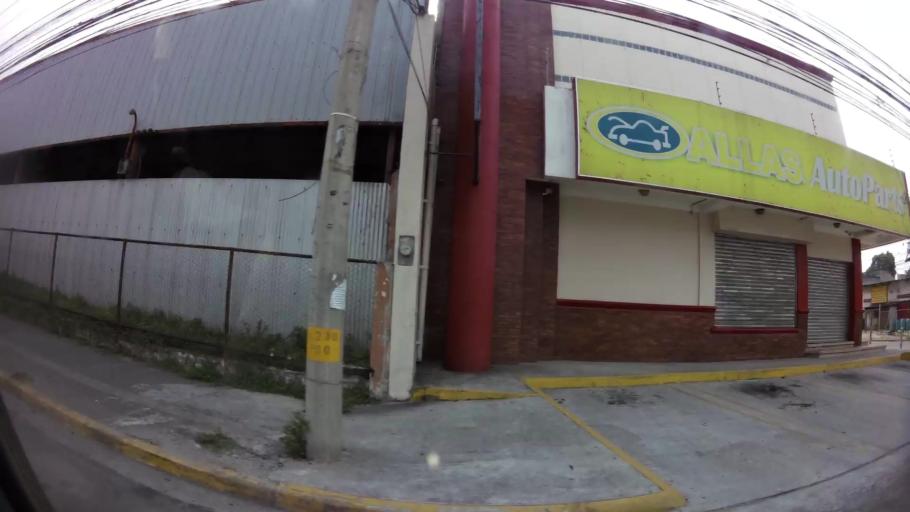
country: HN
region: Cortes
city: San Pedro Sula
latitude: 15.4936
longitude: -88.0259
